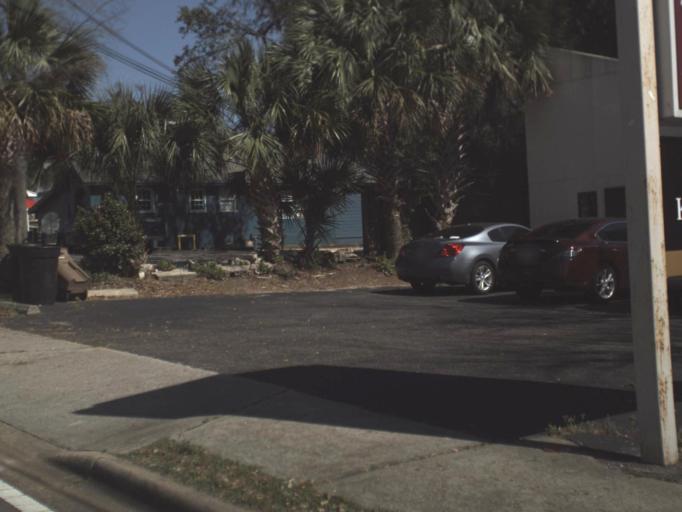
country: US
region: Florida
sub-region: Escambia County
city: East Pensacola Heights
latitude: 30.4253
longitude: -87.1847
